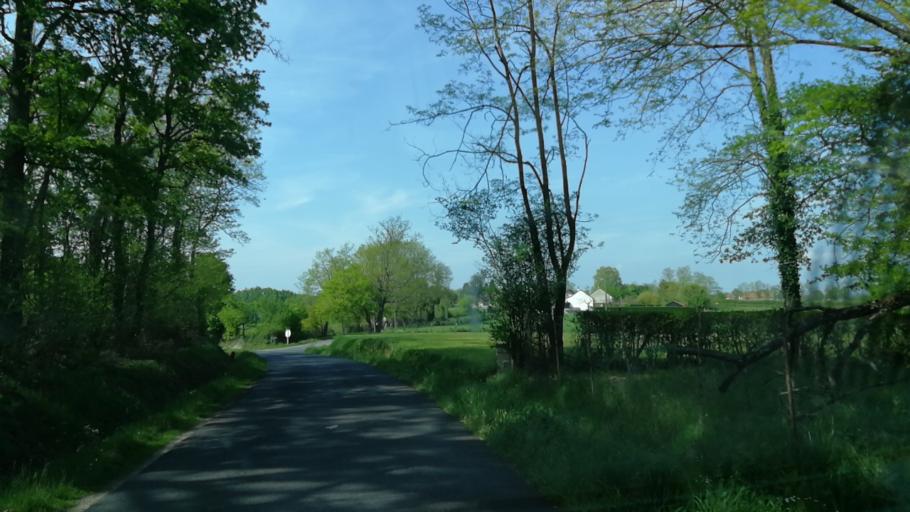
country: FR
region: Auvergne
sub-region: Departement de l'Allier
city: Neuilly-le-Real
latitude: 46.4630
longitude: 3.5415
